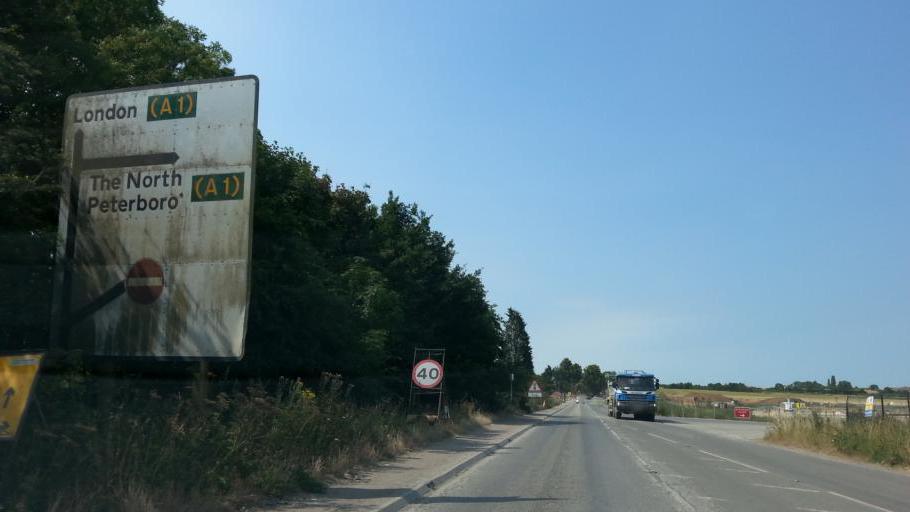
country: GB
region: England
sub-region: Cambridgeshire
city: Brampton
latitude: 52.3073
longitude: -0.2344
